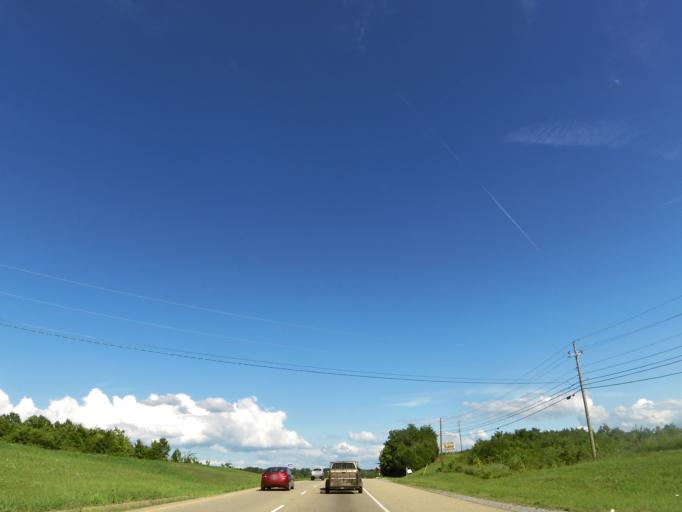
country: US
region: Tennessee
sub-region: Greene County
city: Mosheim
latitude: 36.2228
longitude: -83.0337
